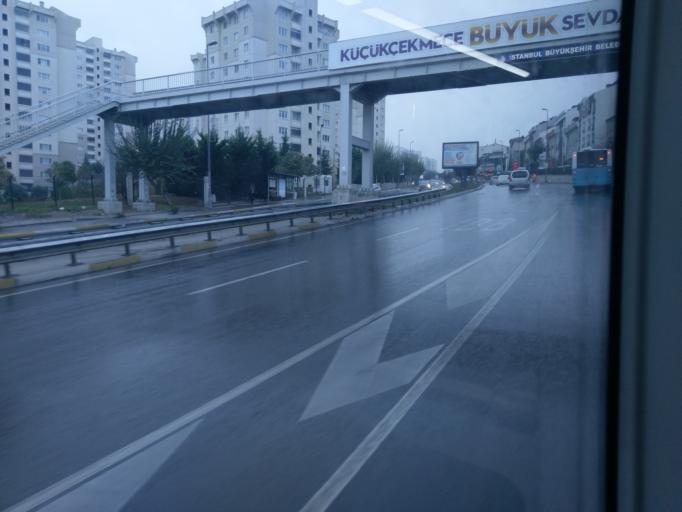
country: TR
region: Istanbul
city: Mahmutbey
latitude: 41.0335
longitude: 28.7709
